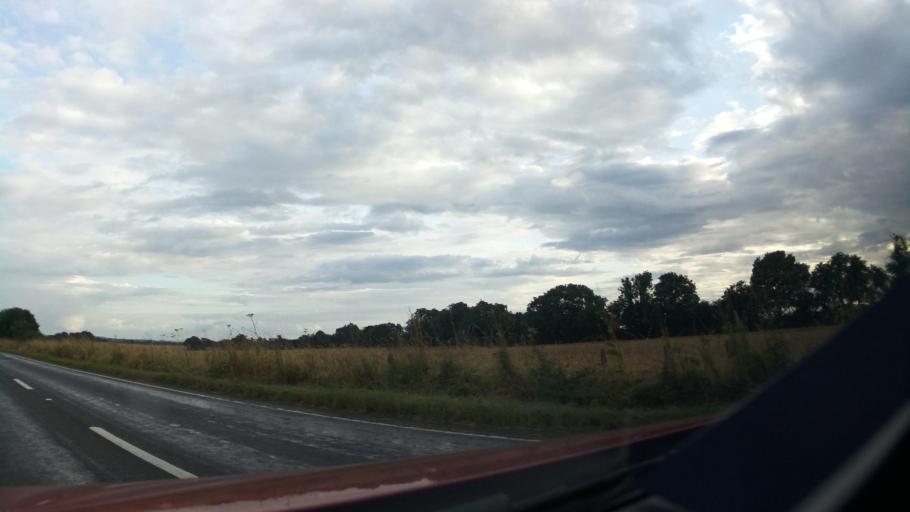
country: GB
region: England
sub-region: Oxfordshire
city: Woodstock
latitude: 51.8957
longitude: -1.3275
